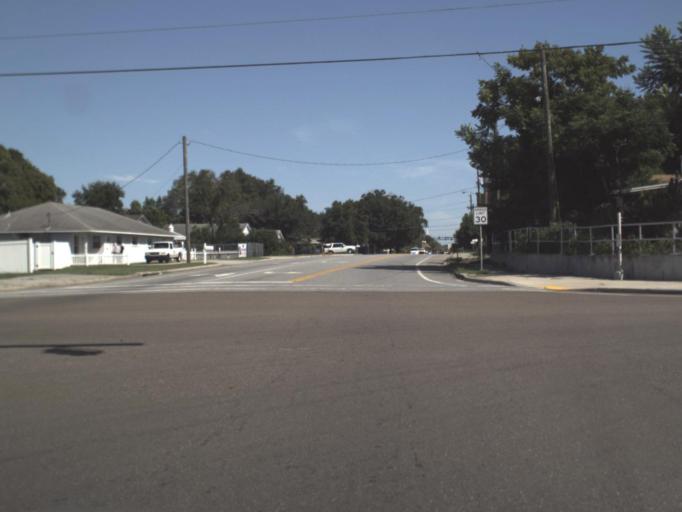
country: US
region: Florida
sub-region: Polk County
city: Auburndale
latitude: 28.0550
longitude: -81.7886
